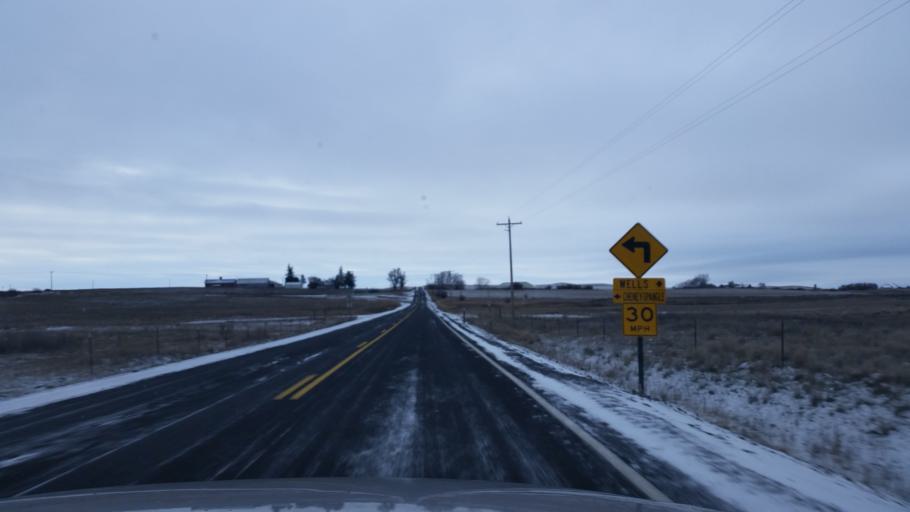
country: US
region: Washington
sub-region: Spokane County
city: Cheney
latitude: 47.3942
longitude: -117.4886
